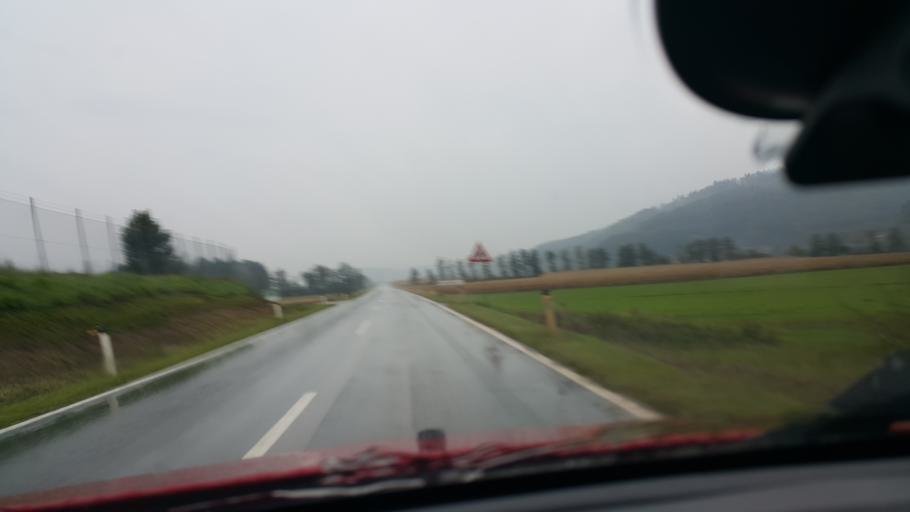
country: AT
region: Carinthia
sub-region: Politischer Bezirk Volkermarkt
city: Ruden
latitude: 46.6558
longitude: 14.8180
